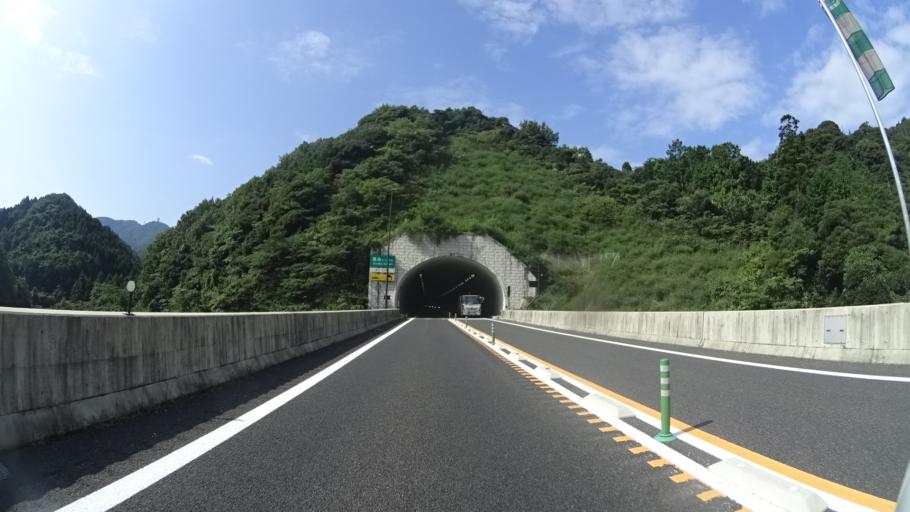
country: JP
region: Shimane
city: Odacho-oda
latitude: 35.1390
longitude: 132.4088
